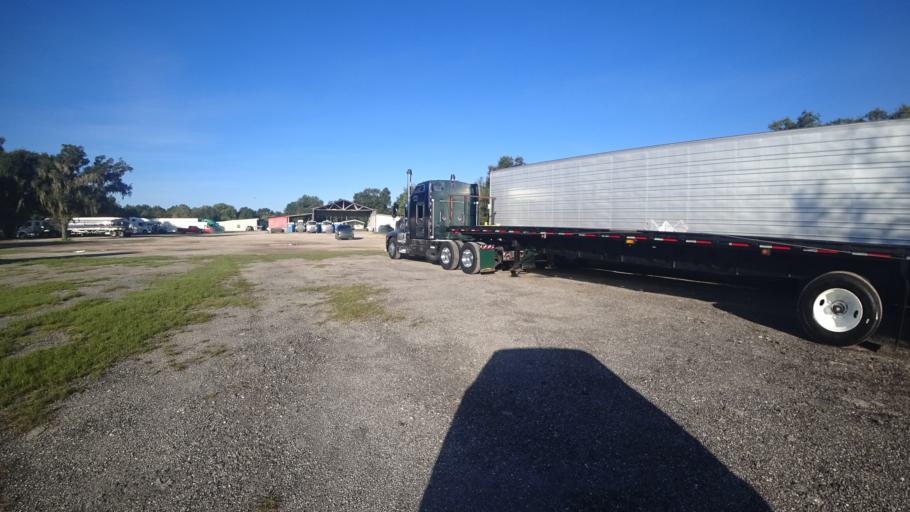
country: US
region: Florida
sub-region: Manatee County
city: Ellenton
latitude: 27.5678
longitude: -82.5217
